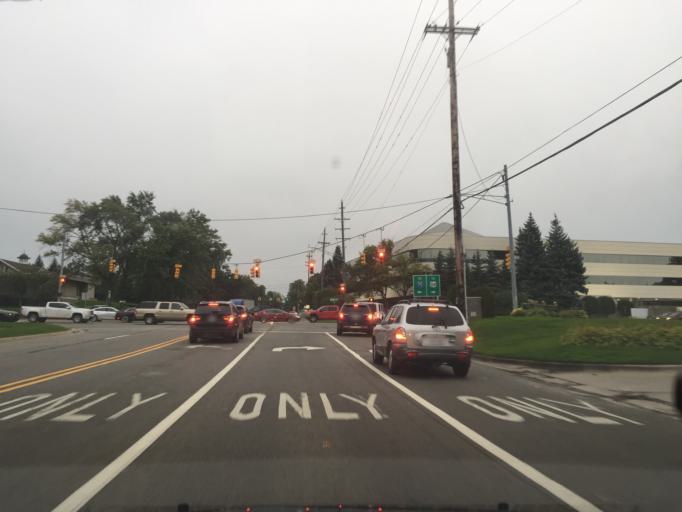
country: US
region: Michigan
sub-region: Oakland County
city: Pontiac
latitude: 42.6037
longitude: -83.2875
